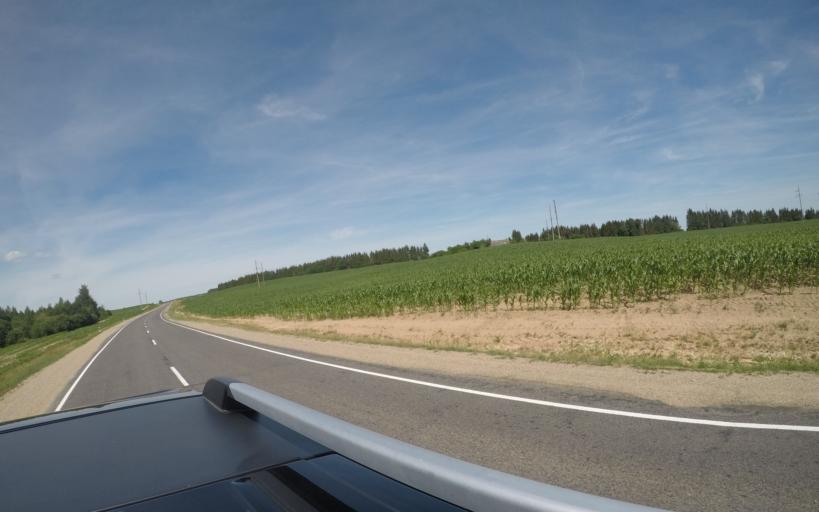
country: BY
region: Grodnenskaya
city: Hal'shany
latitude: 54.2651
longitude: 25.9879
